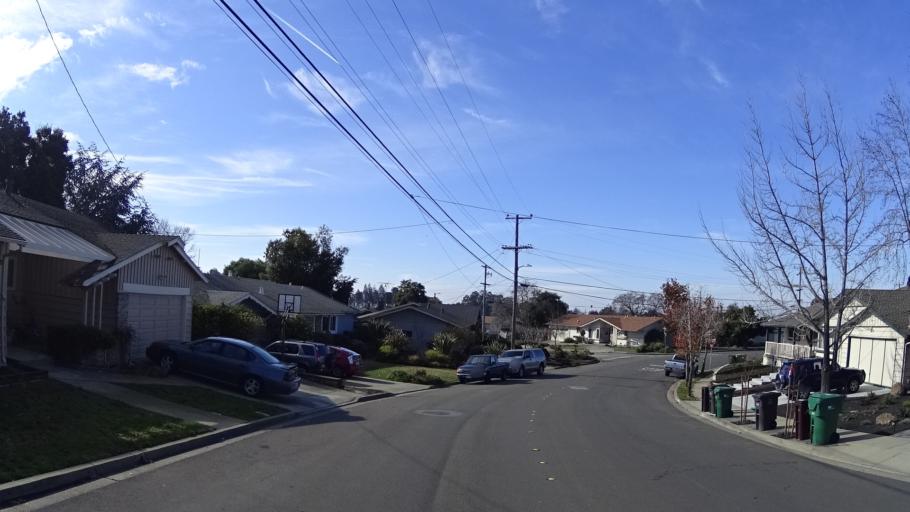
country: US
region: California
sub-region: Alameda County
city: Fairview
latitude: 37.6631
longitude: -122.0501
